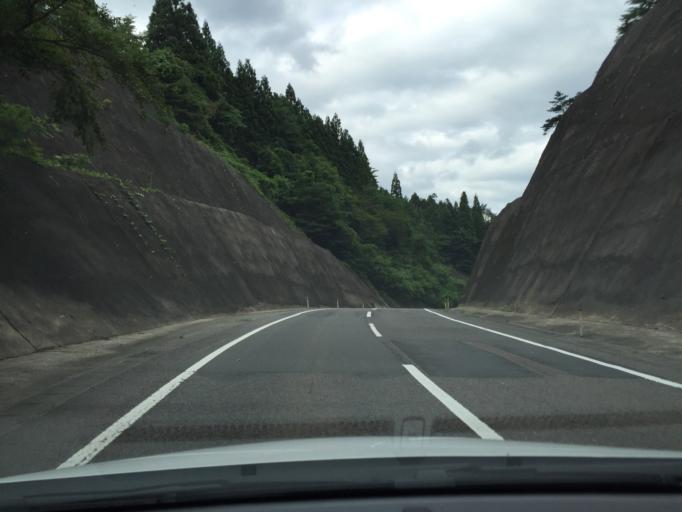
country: JP
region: Fukushima
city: Sukagawa
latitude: 37.1769
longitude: 140.1745
